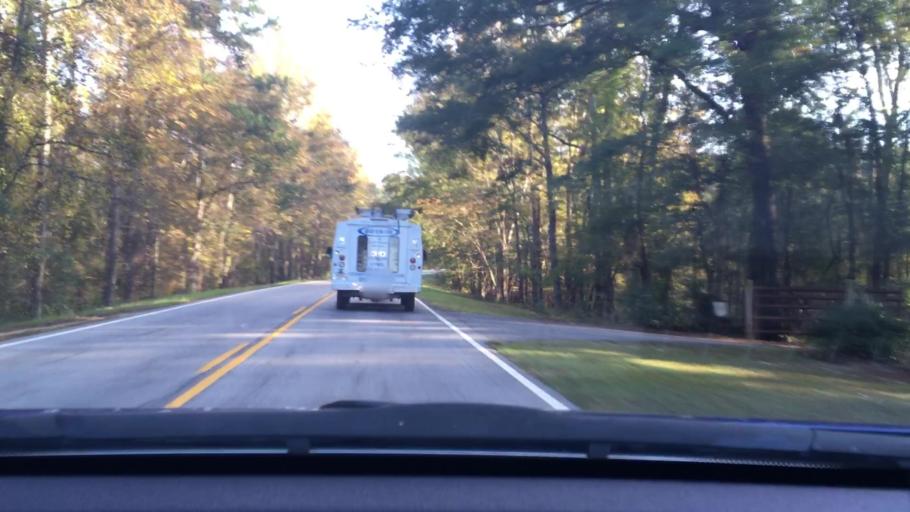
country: US
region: South Carolina
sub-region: Sumter County
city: East Sumter
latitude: 34.0365
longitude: -80.2679
